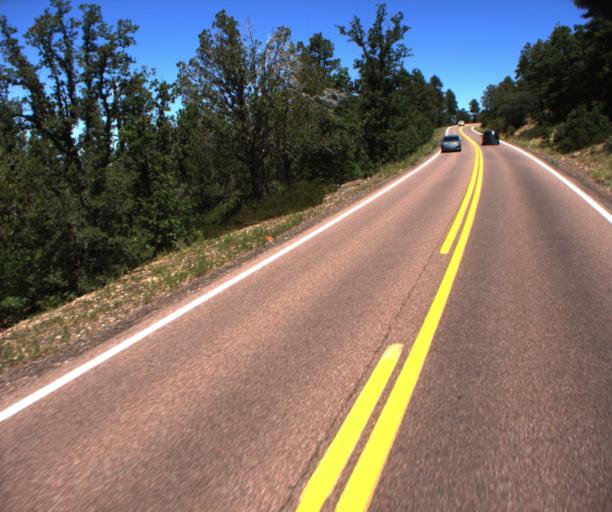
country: US
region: Arizona
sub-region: Gila County
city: Pine
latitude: 34.4274
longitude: -111.5099
